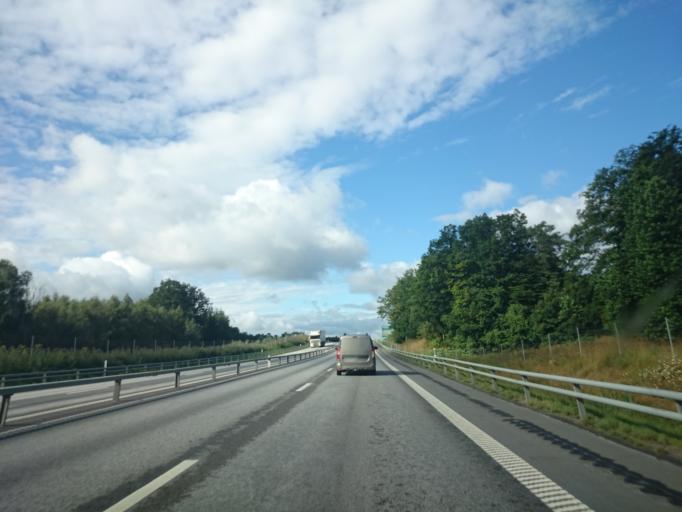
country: SE
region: Skane
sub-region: Horby Kommun
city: Hoerby
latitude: 55.9161
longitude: 13.7766
